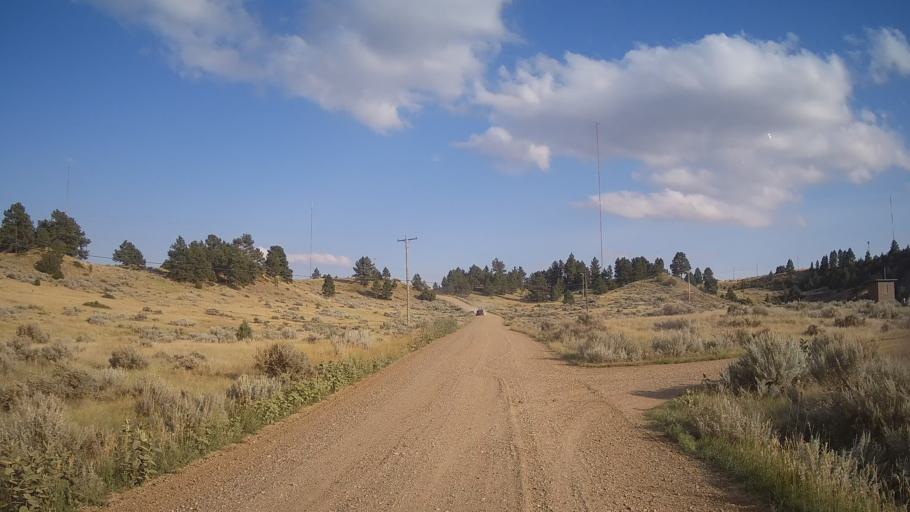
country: US
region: Montana
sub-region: Dawson County
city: Glendive
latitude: 47.0553
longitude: -104.6804
